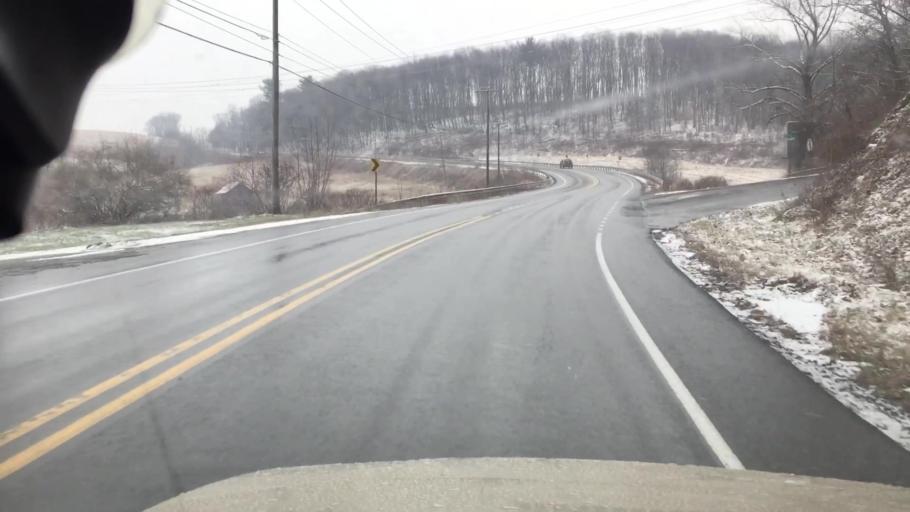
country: US
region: Pennsylvania
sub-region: Luzerne County
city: Nescopeck
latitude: 41.0544
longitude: -76.1757
